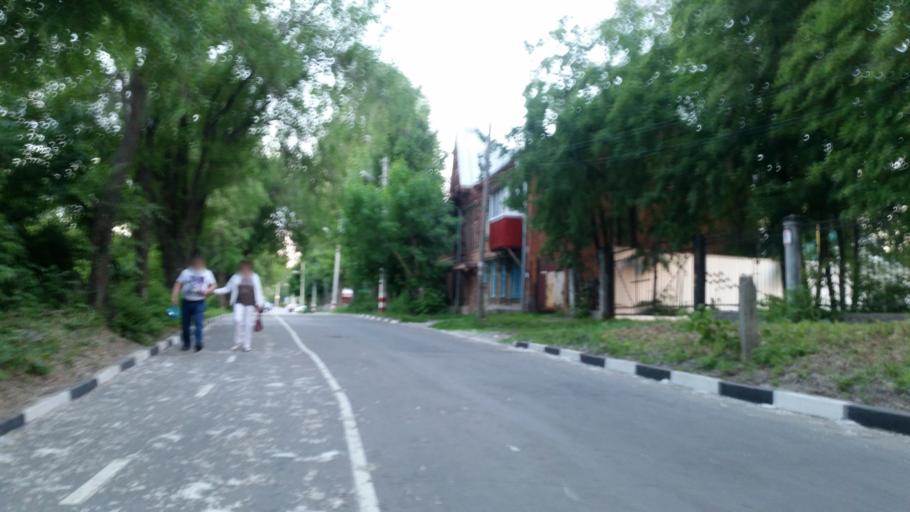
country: RU
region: Ulyanovsk
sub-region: Ulyanovskiy Rayon
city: Ulyanovsk
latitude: 54.3265
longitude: 48.4089
